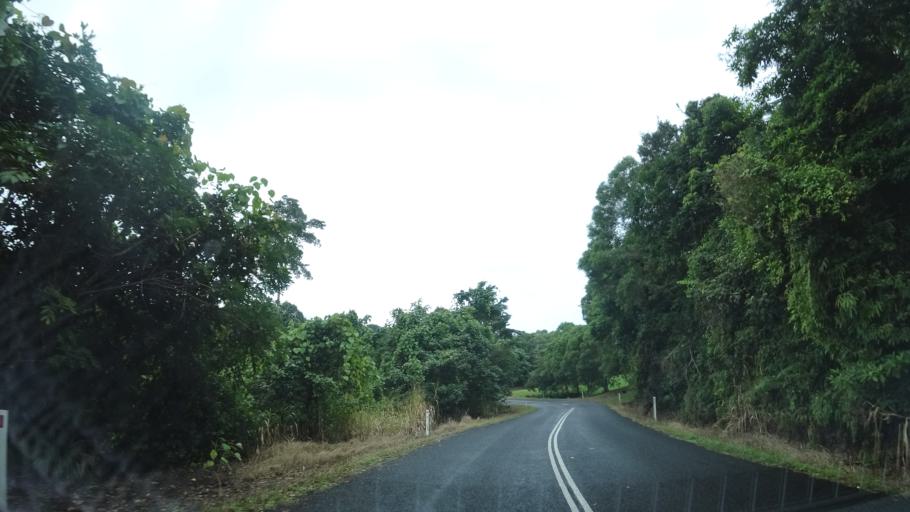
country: AU
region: Queensland
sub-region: Cassowary Coast
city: Innisfail
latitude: -17.5571
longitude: 146.0866
